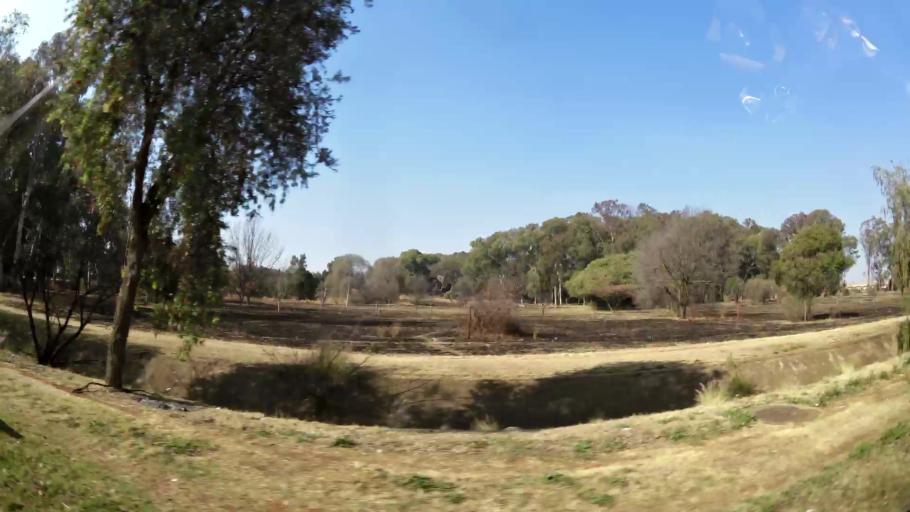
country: ZA
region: Gauteng
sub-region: West Rand District Municipality
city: Randfontein
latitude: -26.1692
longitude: 27.6891
